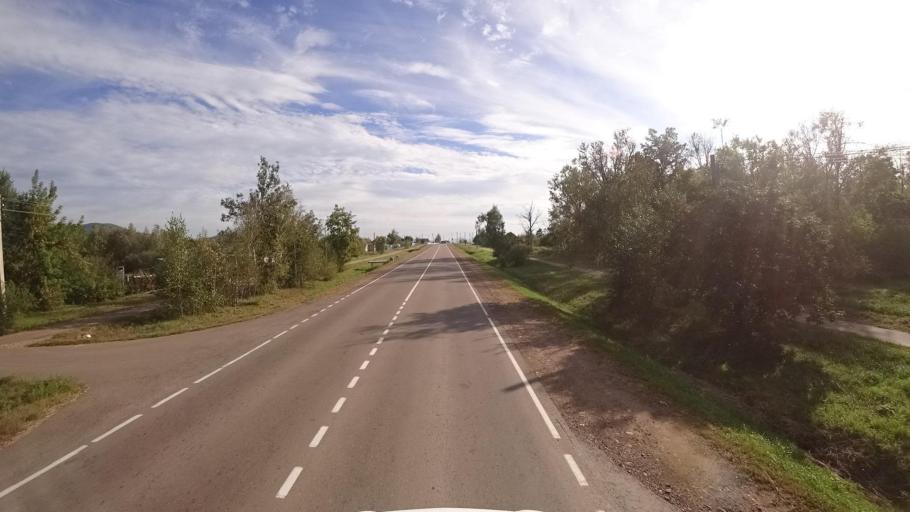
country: RU
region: Primorskiy
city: Dostoyevka
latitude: 44.3039
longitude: 133.4499
